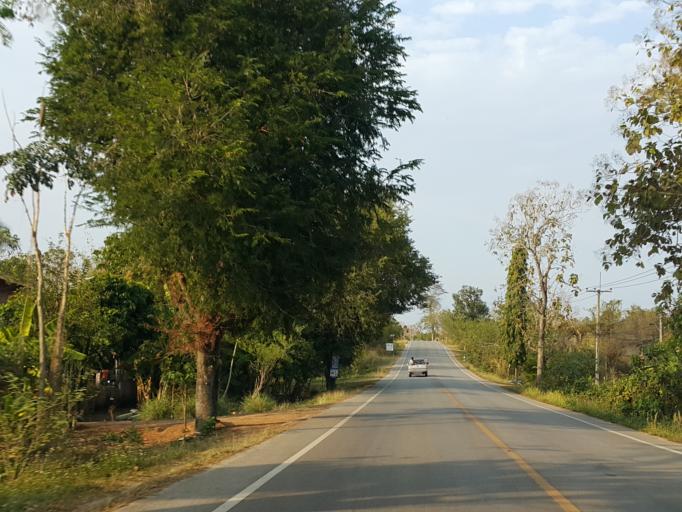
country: TH
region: Lampang
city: Lampang
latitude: 18.5094
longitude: 99.4746
